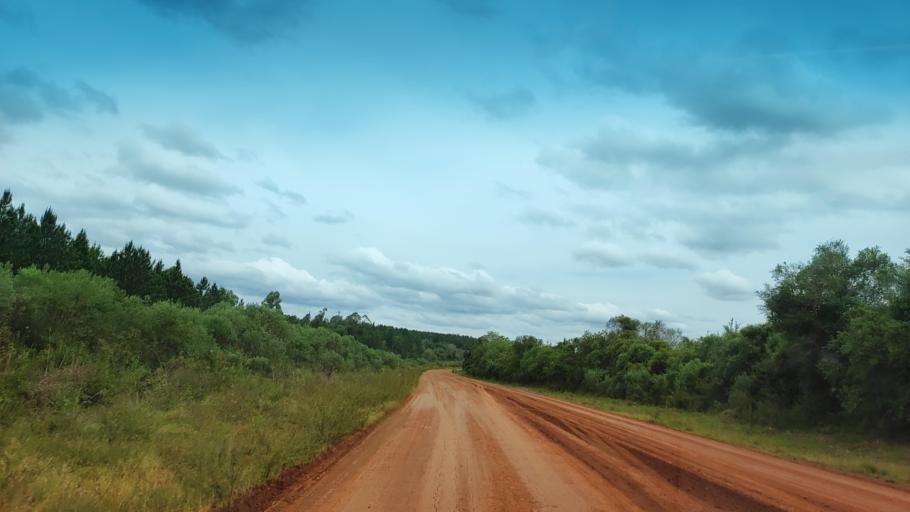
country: AR
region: Misiones
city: Garupa
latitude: -27.5014
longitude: -55.9707
